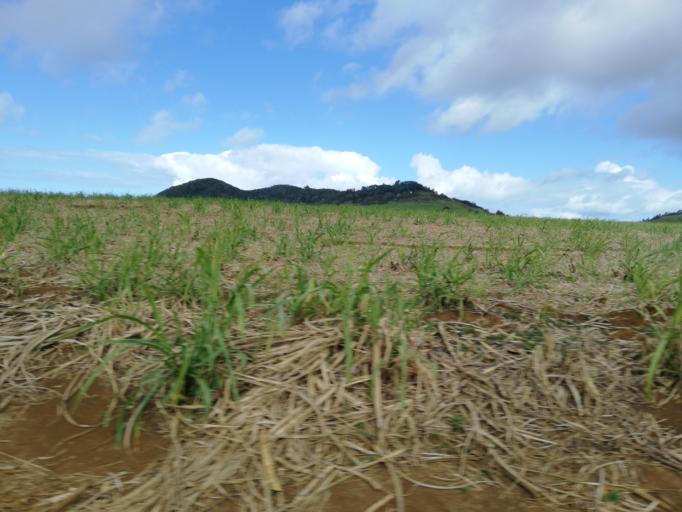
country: MU
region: Flacq
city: Grande Riviere Sud Est
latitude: -20.2831
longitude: 57.7557
